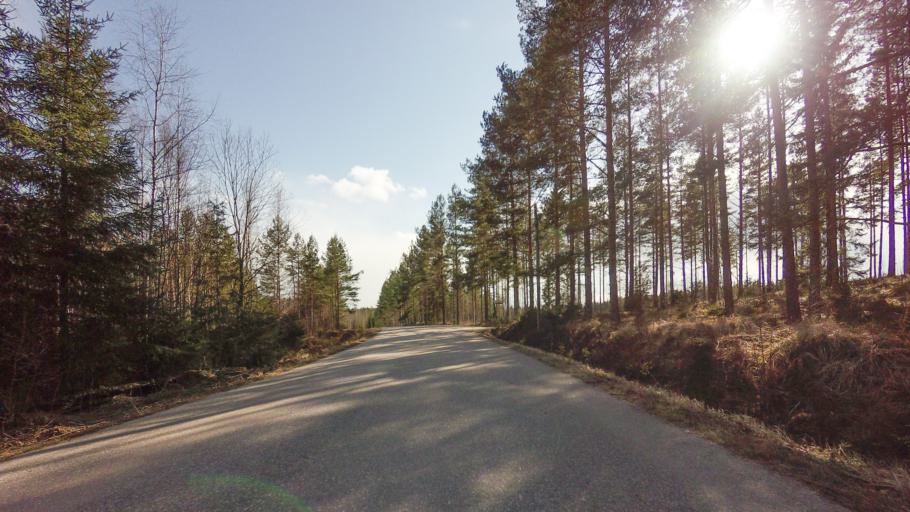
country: FI
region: Varsinais-Suomi
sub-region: Salo
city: Suomusjaervi
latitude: 60.3292
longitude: 23.6487
